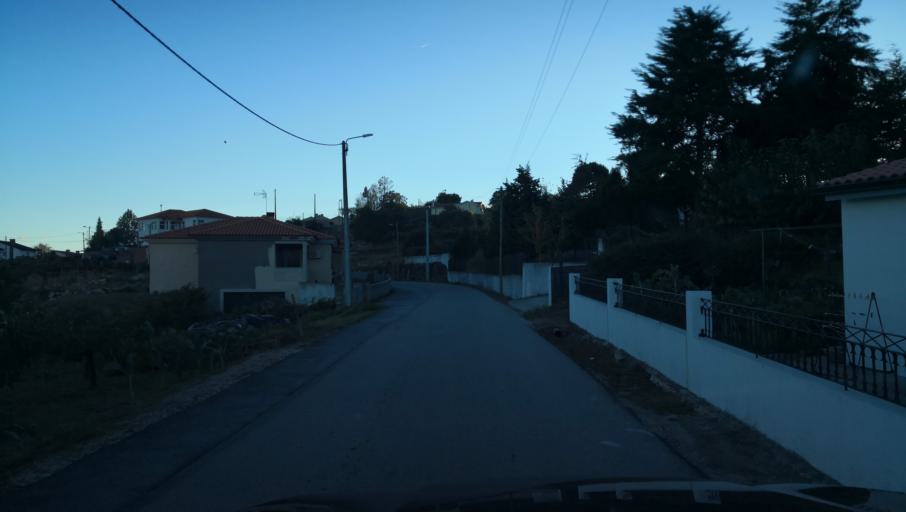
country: PT
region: Vila Real
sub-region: Santa Marta de Penaguiao
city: Santa Marta de Penaguiao
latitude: 41.2593
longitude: -7.7817
